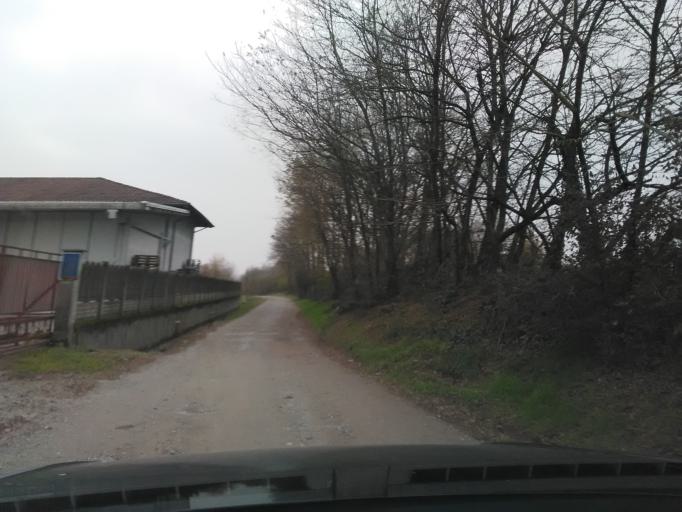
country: IT
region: Piedmont
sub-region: Provincia di Vercelli
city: Santhia
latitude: 45.3695
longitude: 8.1506
